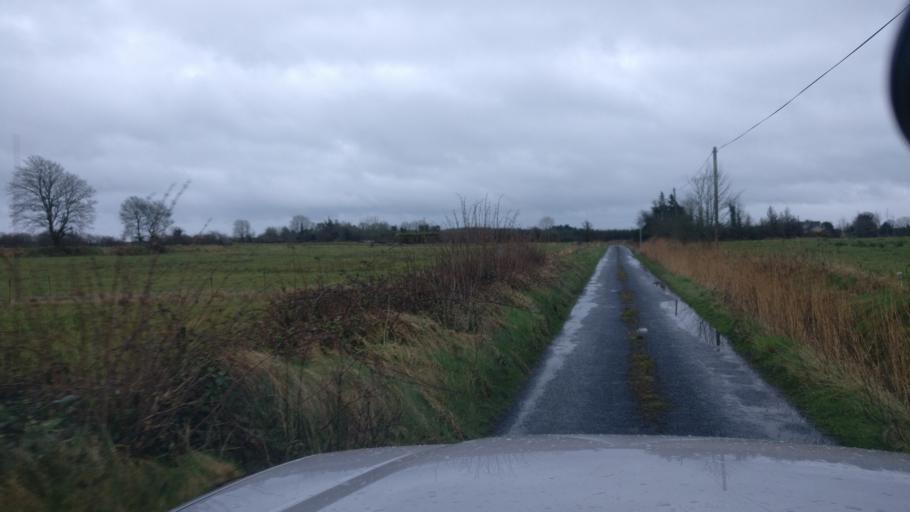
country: IE
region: Connaught
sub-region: County Galway
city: Ballinasloe
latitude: 53.2532
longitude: -8.3532
